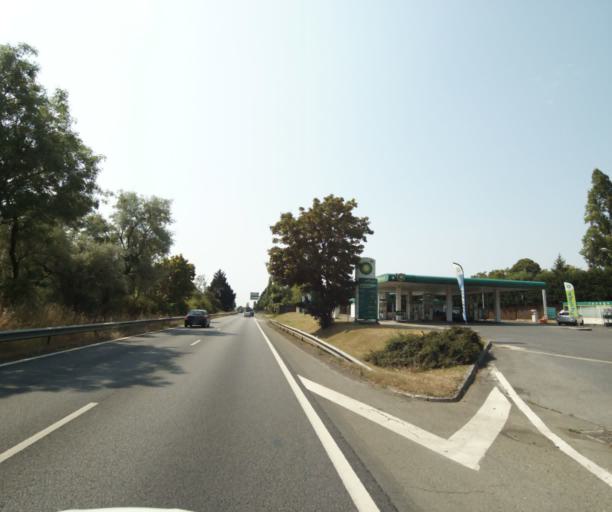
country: FR
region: Ile-de-France
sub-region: Departement des Yvelines
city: Conflans-Sainte-Honorine
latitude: 48.9955
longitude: 2.0807
